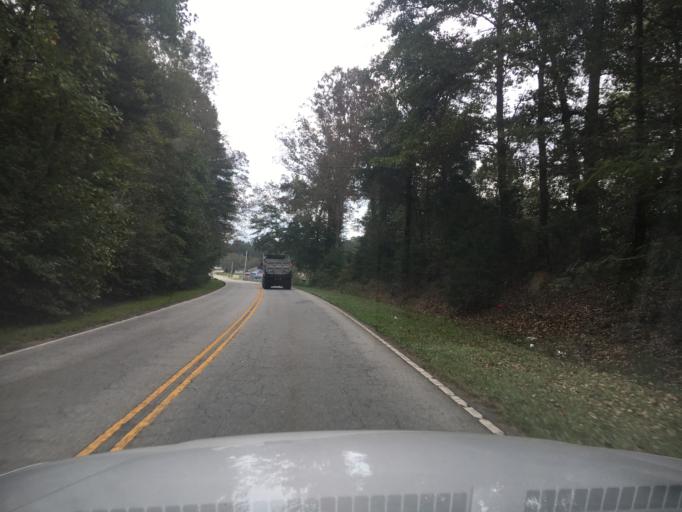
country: US
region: South Carolina
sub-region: Greenville County
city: Greer
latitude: 35.0045
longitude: -82.2556
